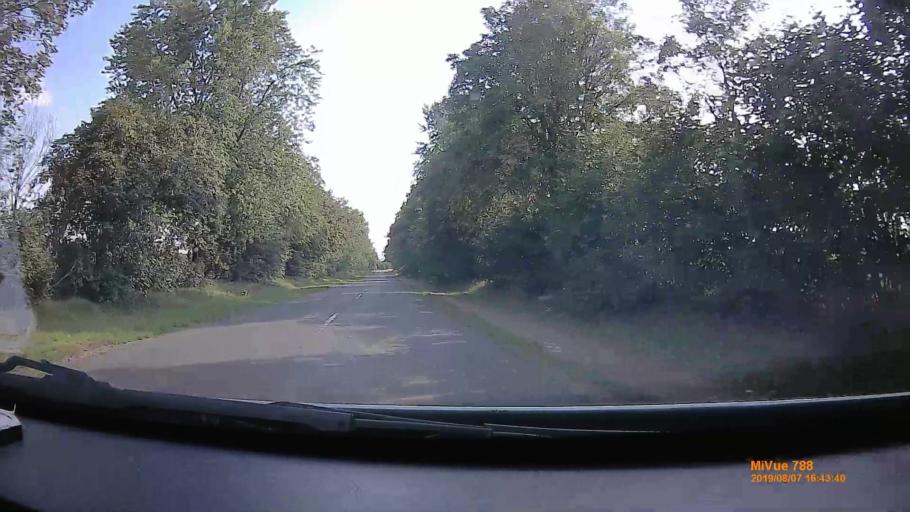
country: HU
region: Borsod-Abauj-Zemplen
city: Abaujszanto
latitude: 48.3534
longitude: 21.2137
